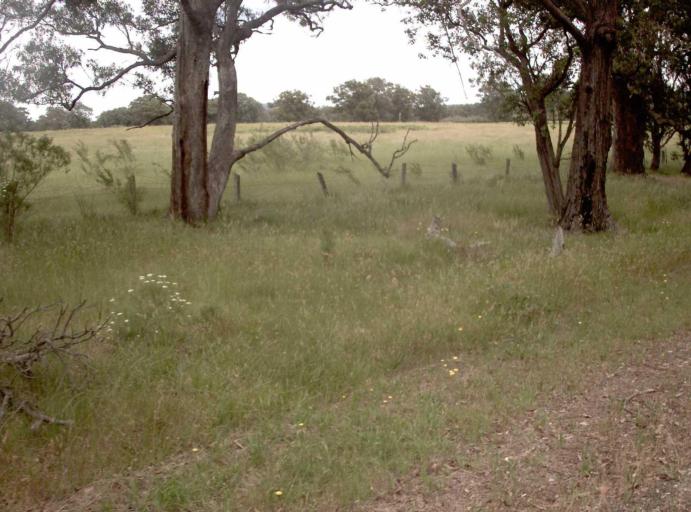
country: AU
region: Victoria
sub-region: East Gippsland
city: Bairnsdale
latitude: -37.7871
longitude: 147.3248
